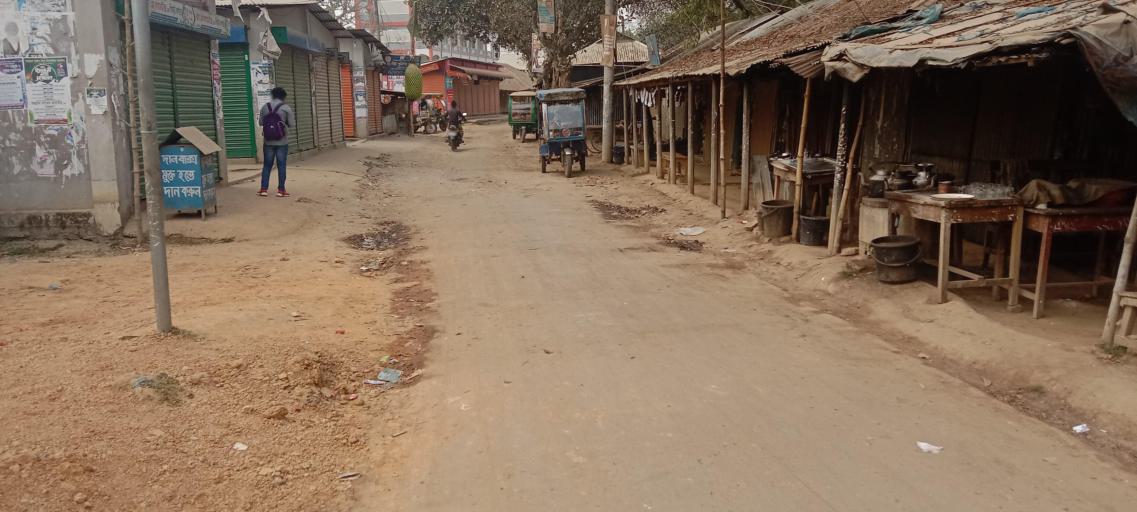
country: BD
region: Dhaka
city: Sakhipur
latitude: 24.4553
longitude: 90.3295
